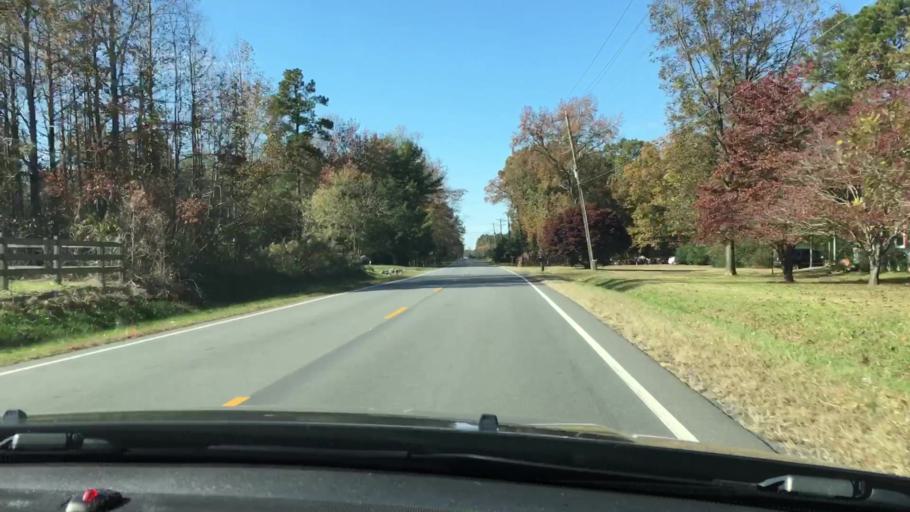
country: US
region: Virginia
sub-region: King William County
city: King William
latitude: 37.6887
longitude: -77.0191
